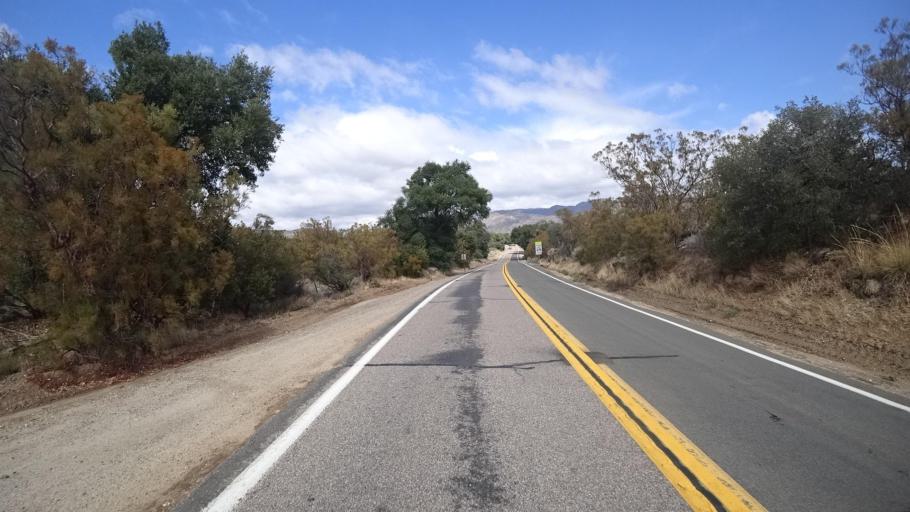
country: US
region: California
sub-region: San Diego County
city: Pine Valley
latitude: 32.7306
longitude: -116.4954
